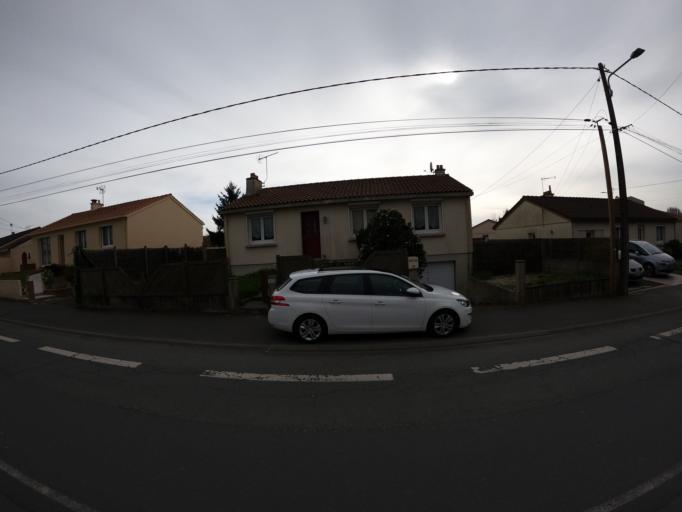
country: FR
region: Pays de la Loire
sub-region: Departement de la Vendee
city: Montaigu
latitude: 46.9819
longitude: -1.3047
